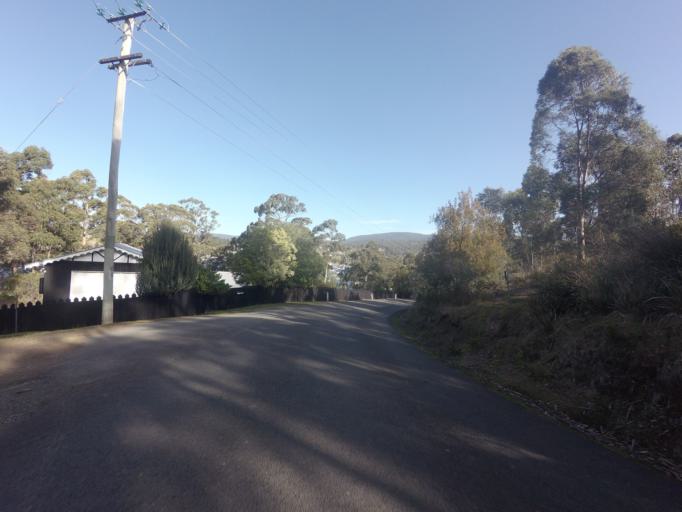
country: AU
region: Tasmania
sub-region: Kingborough
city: Kettering
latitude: -43.1215
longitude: 147.2558
